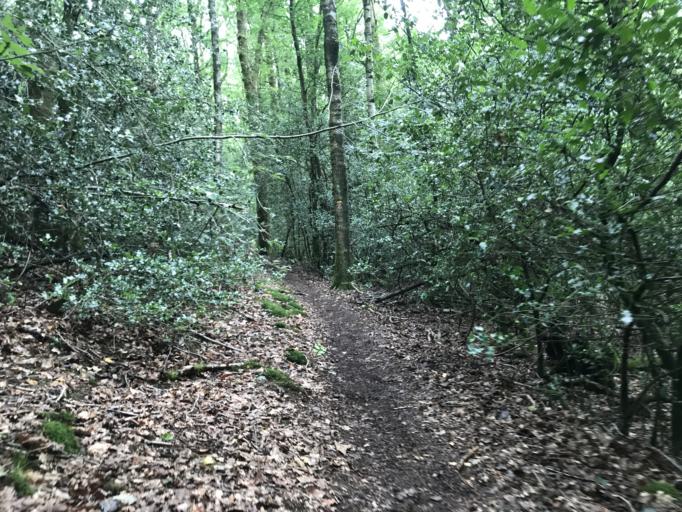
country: FR
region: Champagne-Ardenne
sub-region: Departement des Ardennes
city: Montherme
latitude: 49.8919
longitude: 4.7515
